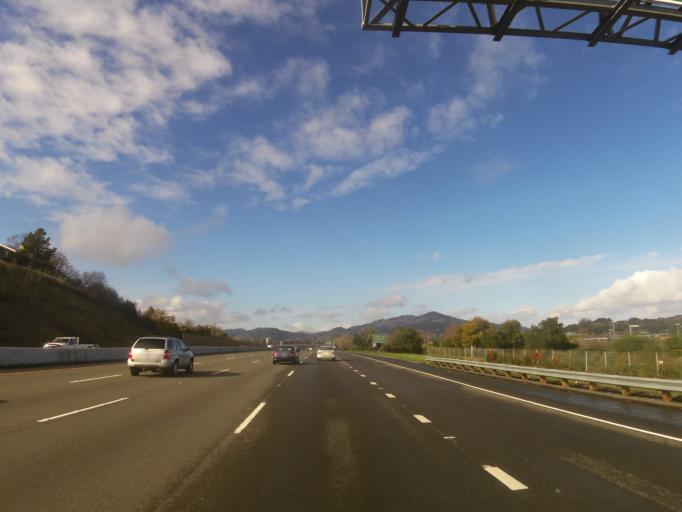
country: US
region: California
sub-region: Marin County
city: Novato
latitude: 38.0855
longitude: -122.5520
